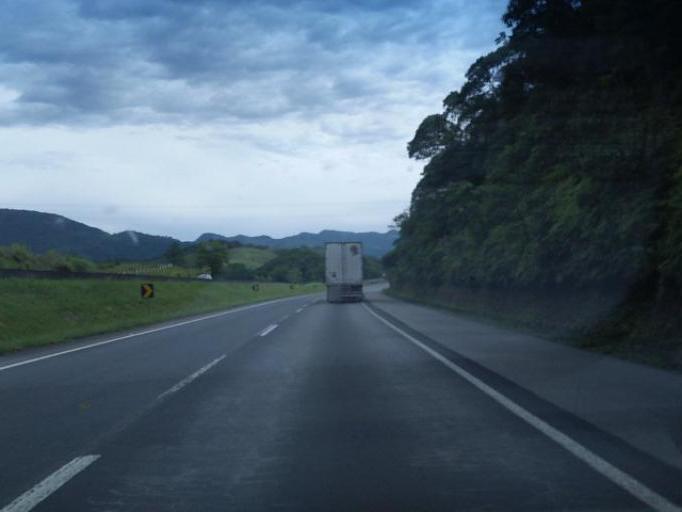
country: BR
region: Sao Paulo
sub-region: Miracatu
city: Miracatu
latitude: -24.2409
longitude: -47.3630
